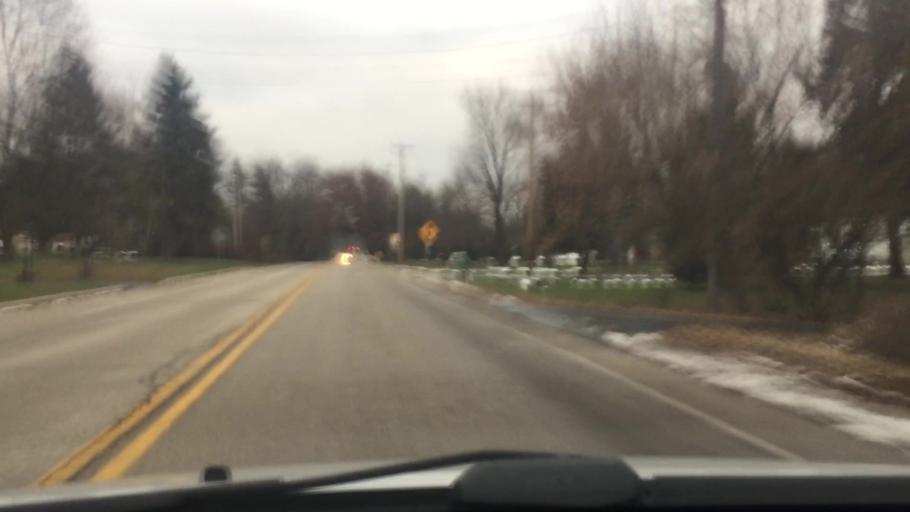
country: US
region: Wisconsin
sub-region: Waukesha County
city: Pewaukee
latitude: 43.0567
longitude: -88.3042
